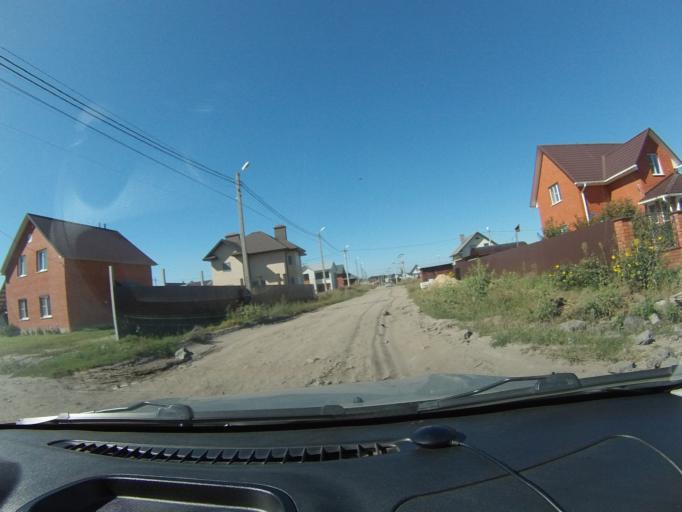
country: RU
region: Tambov
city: Komsomolets
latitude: 52.7780
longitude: 41.3713
